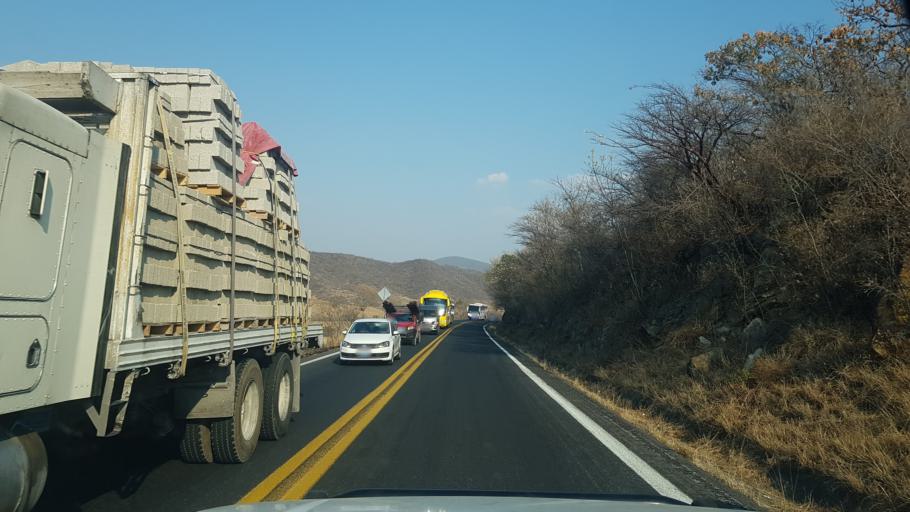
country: MX
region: Puebla
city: Calmeca
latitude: 18.6417
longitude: -98.5919
